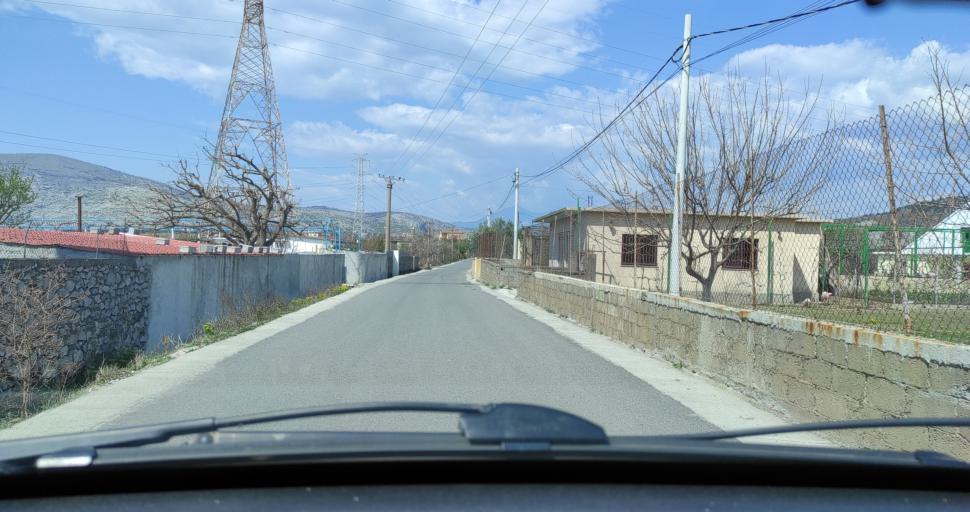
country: AL
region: Shkoder
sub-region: Rrethi i Shkodres
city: Vau i Dejes
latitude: 41.9988
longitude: 19.6432
